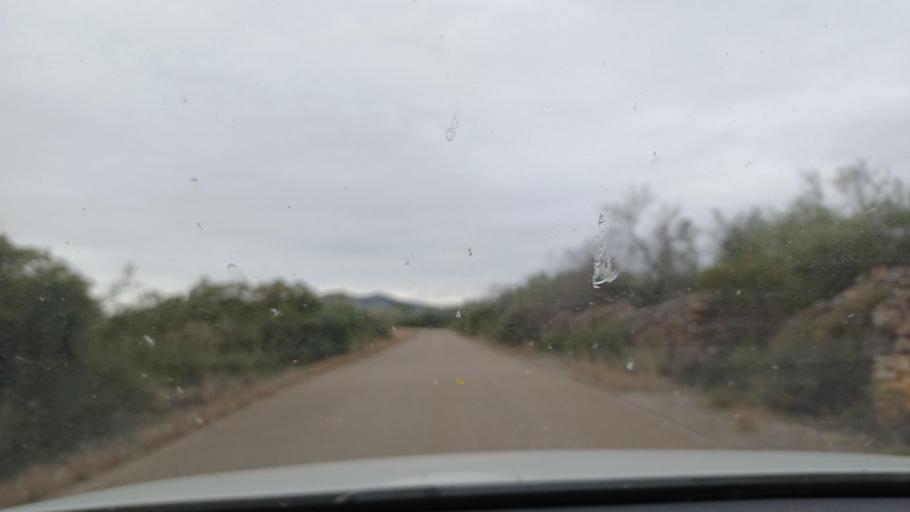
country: ES
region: Valencia
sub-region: Provincia de Castello
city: Canet lo Roig
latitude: 40.5853
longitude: 0.2852
